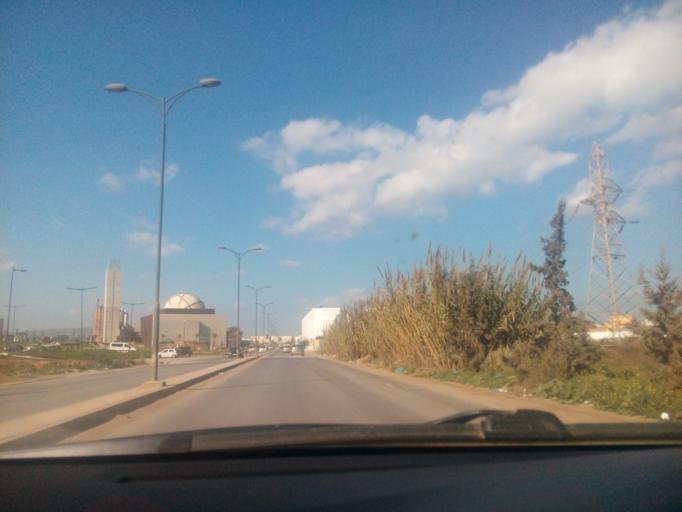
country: DZ
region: Oran
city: Es Senia
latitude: 35.6778
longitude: -0.5982
